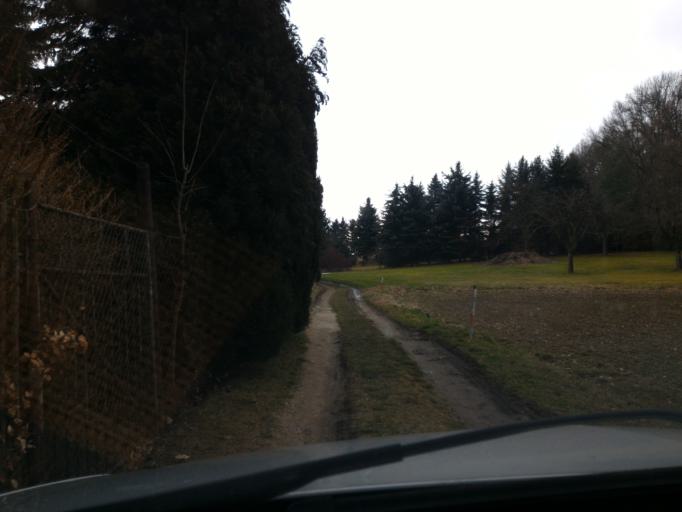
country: DE
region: Saxony
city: Grossschonau
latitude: 50.9040
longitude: 14.6662
